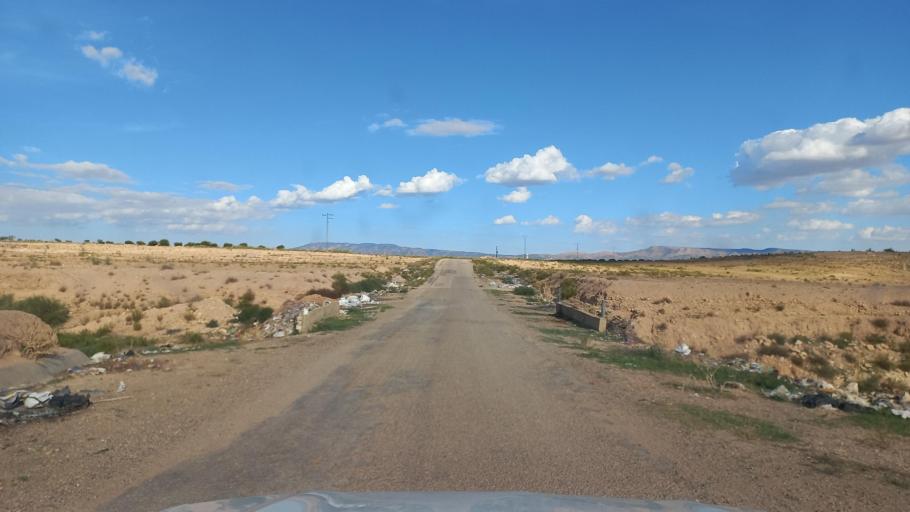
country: TN
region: Al Qasrayn
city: Sbiba
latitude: 35.3924
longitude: 9.0215
